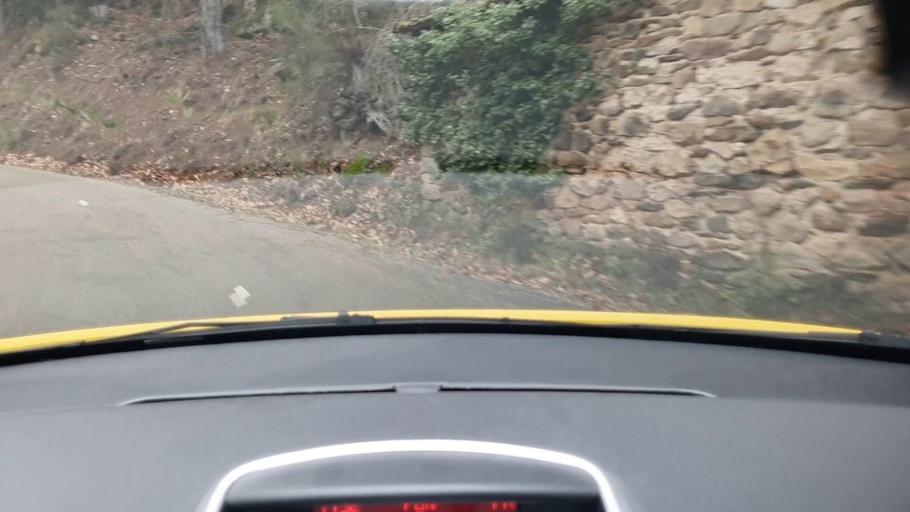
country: FR
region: Languedoc-Roussillon
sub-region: Departement du Gard
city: Besseges
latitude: 44.3520
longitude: 4.0203
